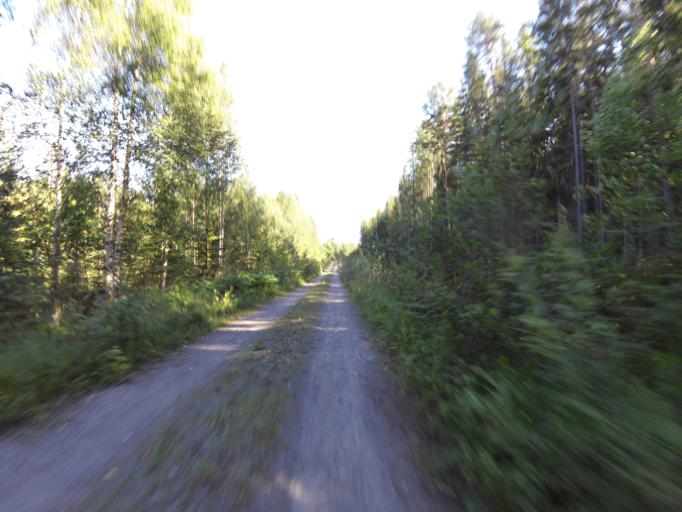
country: SE
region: Gaevleborg
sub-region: Hofors Kommun
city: Hofors
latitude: 60.5470
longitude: 16.4310
